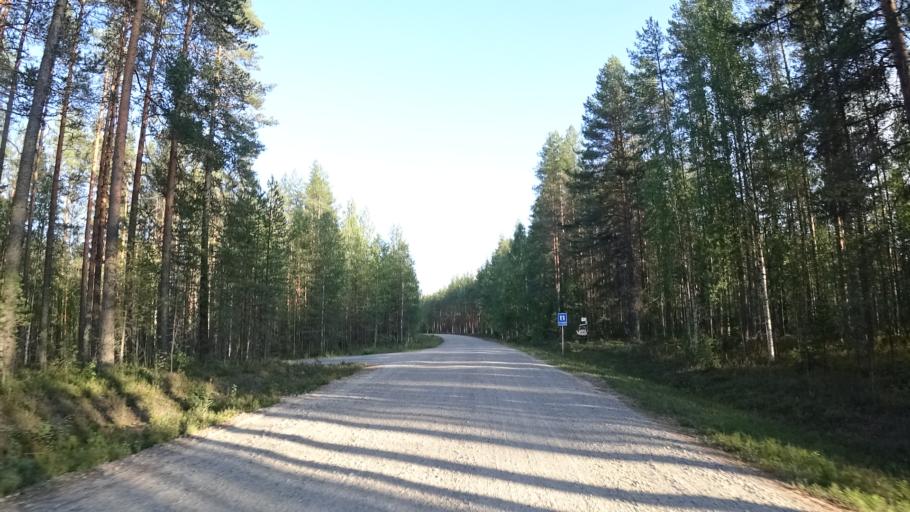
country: FI
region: North Karelia
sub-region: Joensuu
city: Ilomantsi
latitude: 63.1295
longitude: 30.7124
